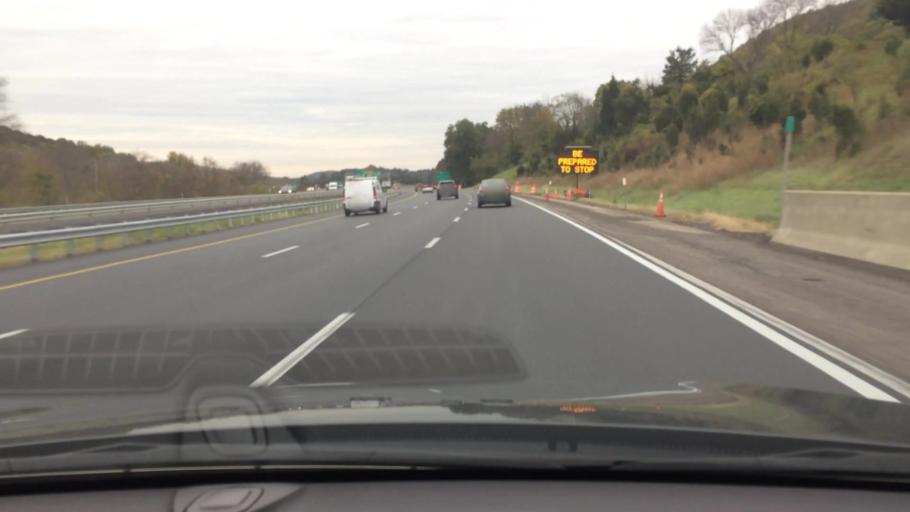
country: US
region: New York
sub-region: Orange County
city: Harriman
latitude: 41.2826
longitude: -74.1430
